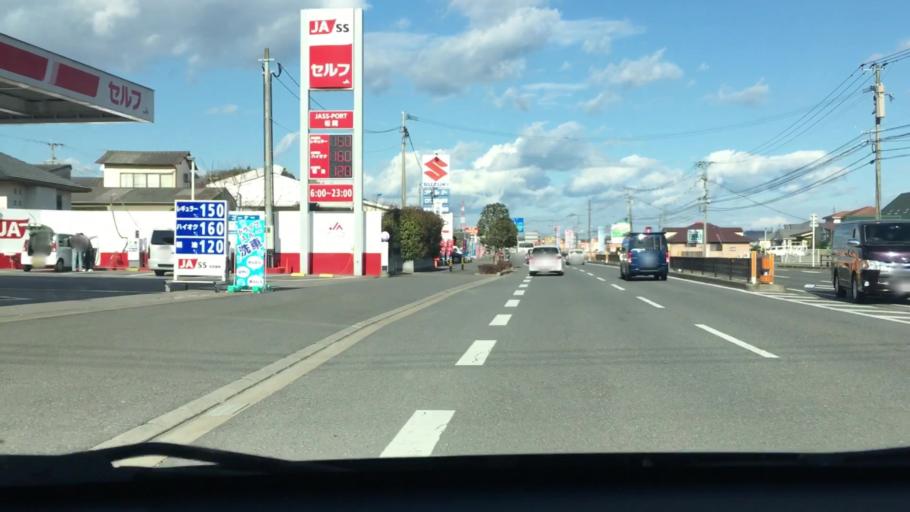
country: JP
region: Oita
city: Tsurusaki
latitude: 33.1885
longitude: 131.6706
